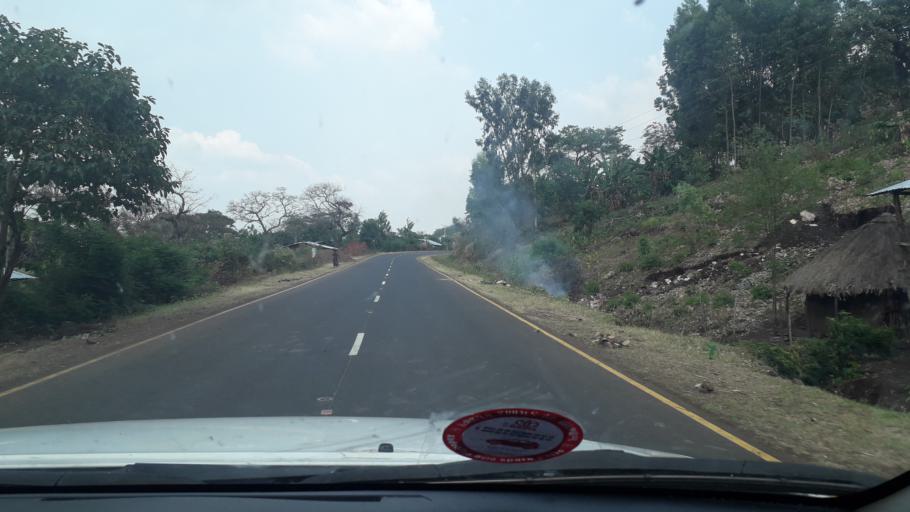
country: ET
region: Southern Nations, Nationalities, and People's Region
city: Mizan Teferi
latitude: 6.7893
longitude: 35.2131
